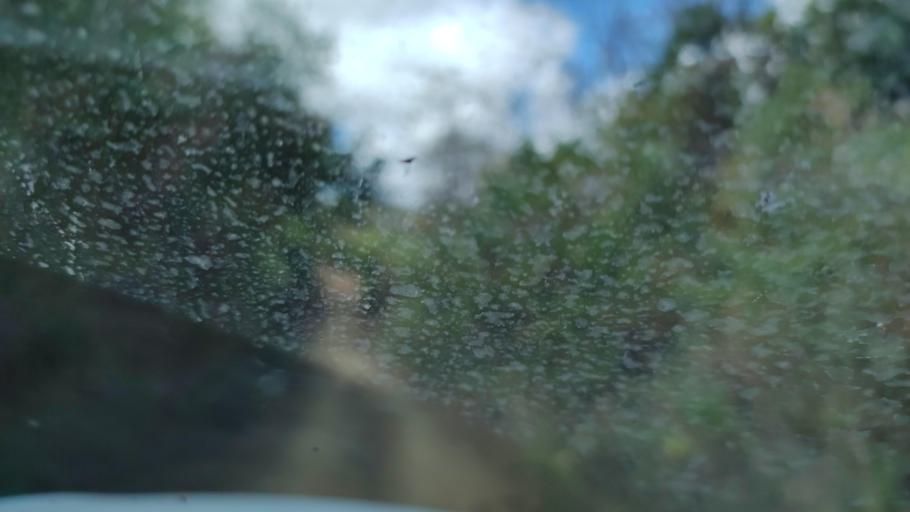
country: NI
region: Carazo
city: Santa Teresa
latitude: 11.6501
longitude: -86.2106
